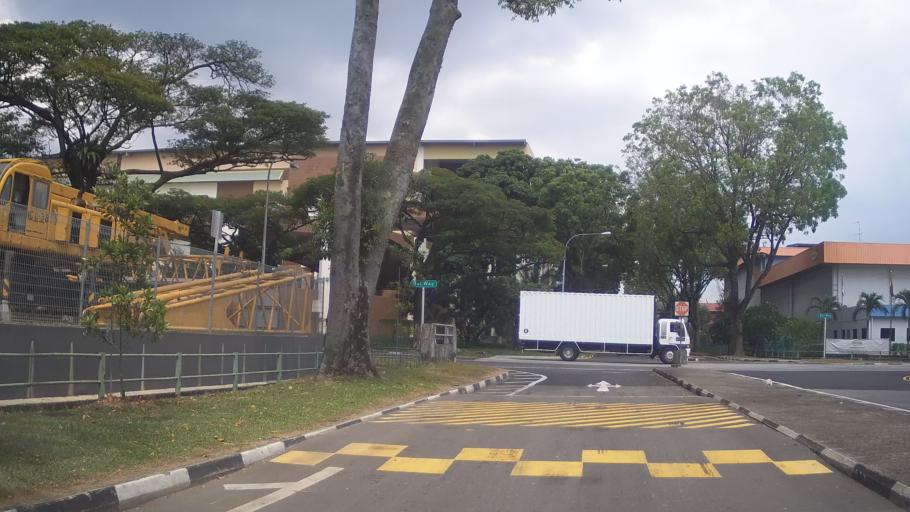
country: MY
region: Johor
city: Johor Bahru
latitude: 1.3148
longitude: 103.6702
